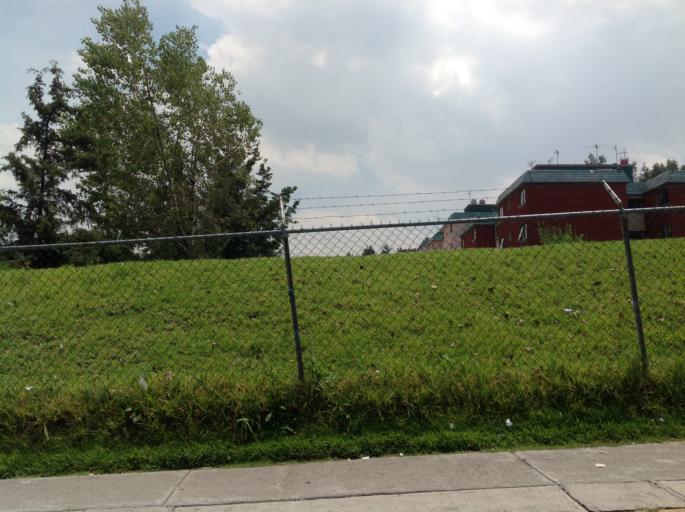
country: MX
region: Mexico
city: Ciudad Lopez Mateos
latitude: 19.6055
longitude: -99.2301
